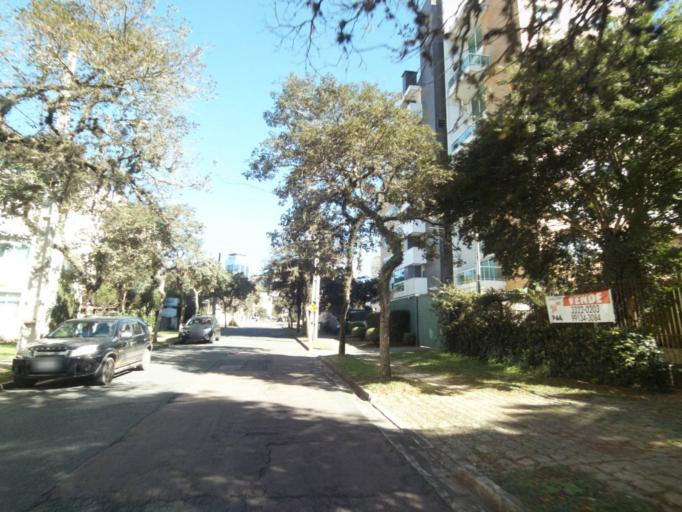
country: BR
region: Parana
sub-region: Curitiba
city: Curitiba
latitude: -25.4160
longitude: -49.2573
